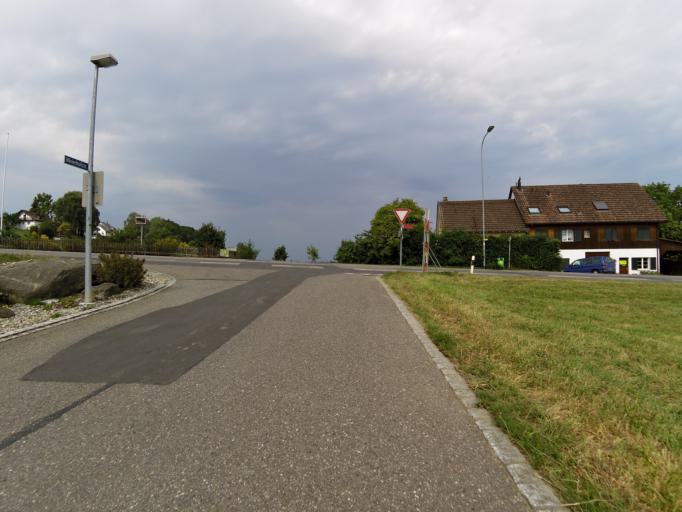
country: CH
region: Thurgau
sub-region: Kreuzlingen District
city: Tagerwilen
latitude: 47.6562
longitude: 9.1241
